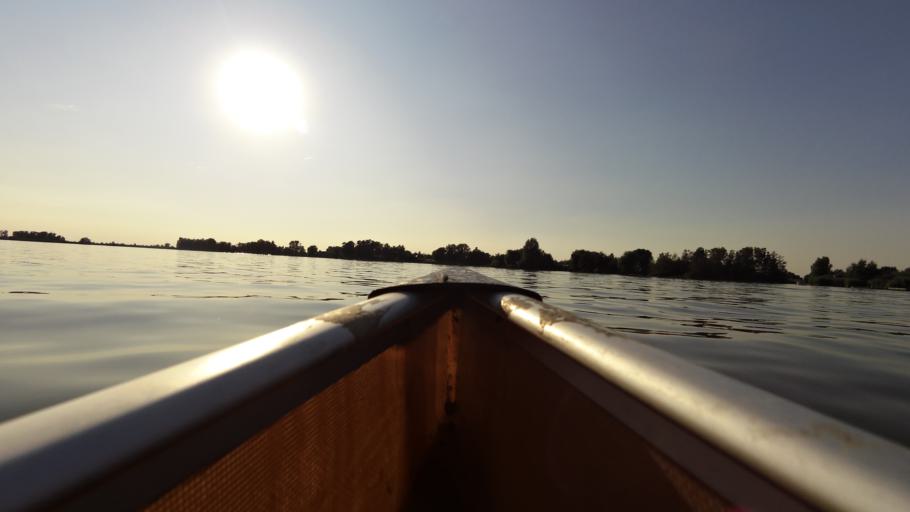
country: NL
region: South Holland
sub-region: Gemeente Nieuwkoop
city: Nieuwkoop
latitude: 52.1296
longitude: 4.7700
